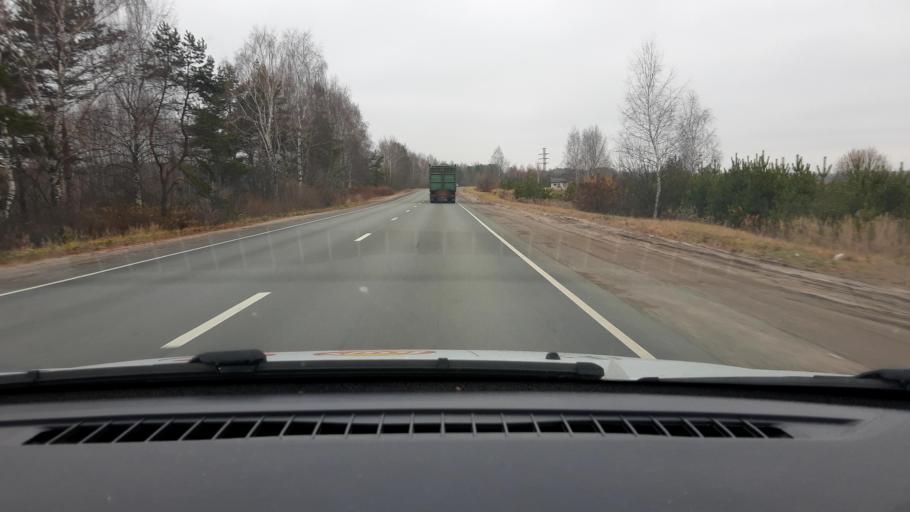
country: RU
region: Nizjnij Novgorod
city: Gidrotorf
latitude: 56.5556
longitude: 43.5083
